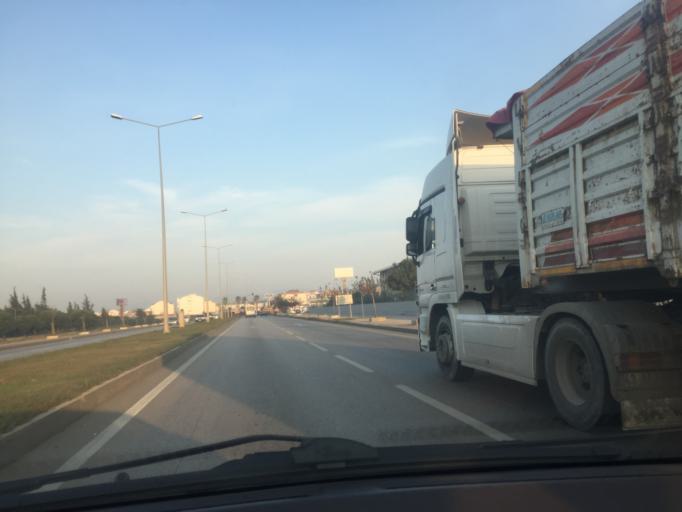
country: TR
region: Balikesir
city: Bandirma
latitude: 40.3319
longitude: 27.9951
